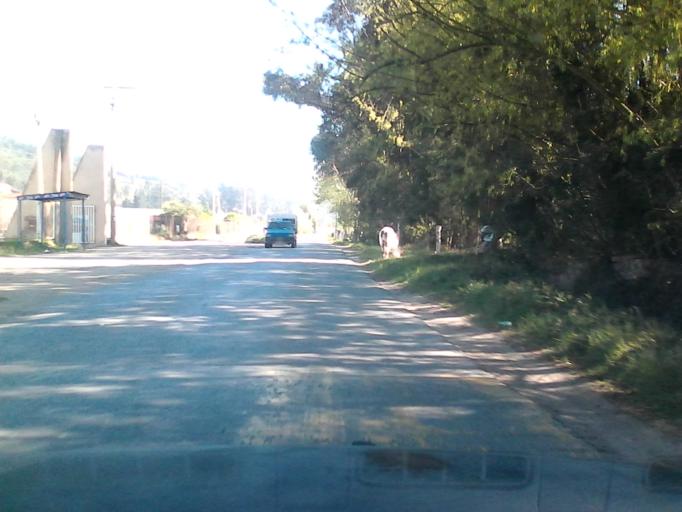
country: CO
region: Boyaca
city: Duitama
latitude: 5.7863
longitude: -73.0508
